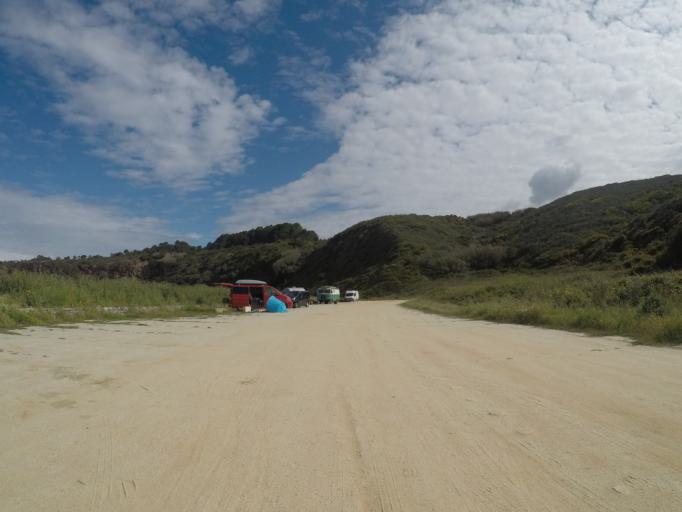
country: PT
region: Beja
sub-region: Odemira
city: Sao Teotonio
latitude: 37.4408
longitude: -8.7952
